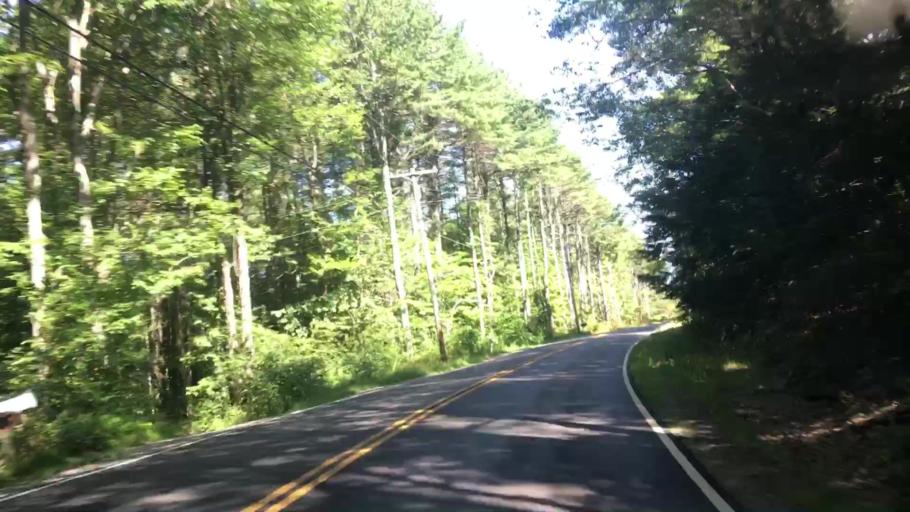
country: US
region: Maine
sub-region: Sagadahoc County
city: Topsham
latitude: 43.9857
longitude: -69.9858
